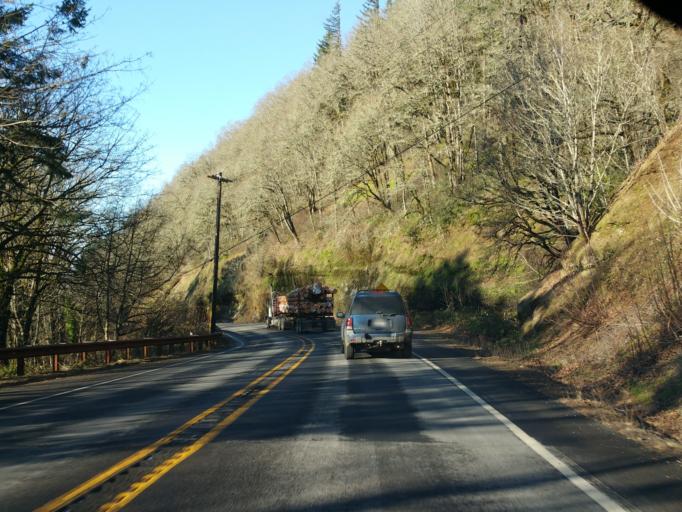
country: US
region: Washington
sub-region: Clark County
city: Washougal
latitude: 45.5597
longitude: -122.2492
